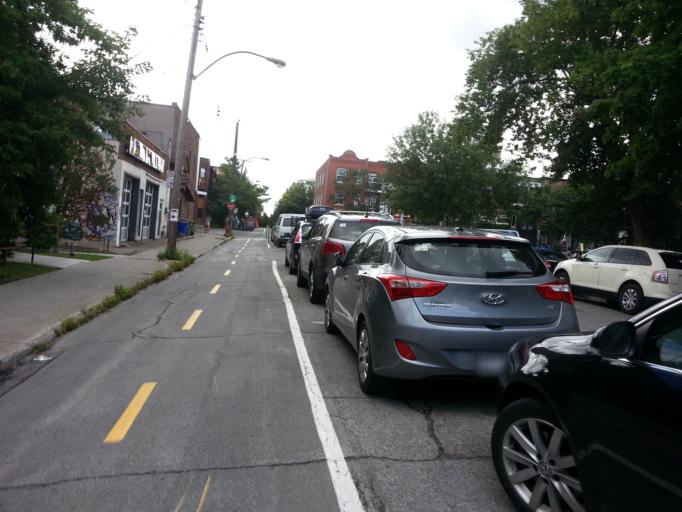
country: CA
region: Quebec
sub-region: Montreal
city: Montreal
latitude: 45.5229
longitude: -73.5941
